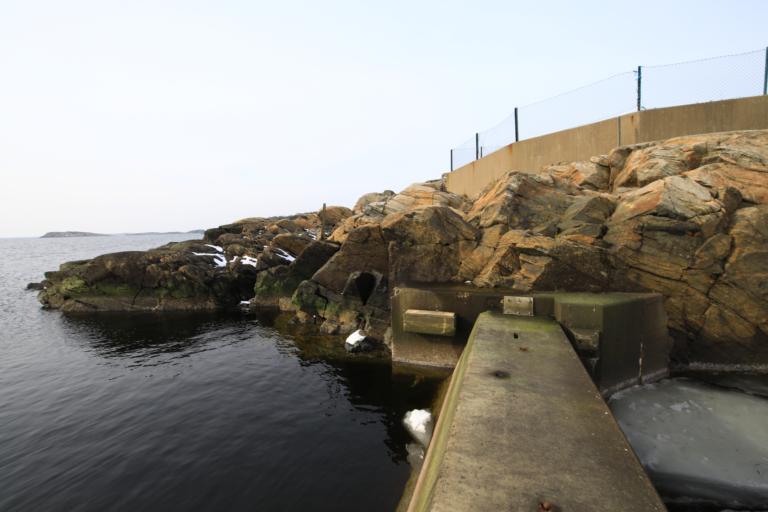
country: SE
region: Halland
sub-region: Kungsbacka Kommun
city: Frillesas
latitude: 57.2139
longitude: 12.1611
